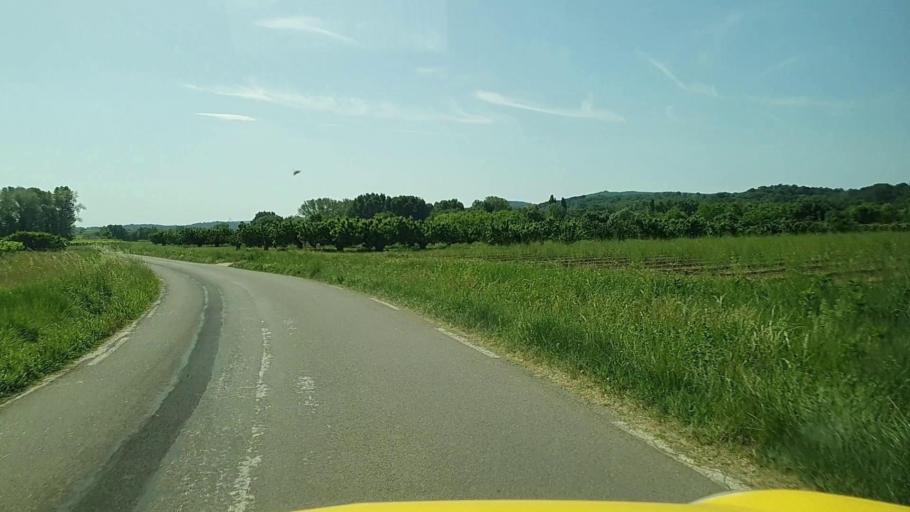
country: FR
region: Languedoc-Roussillon
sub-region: Departement du Gard
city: Sabran
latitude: 44.1070
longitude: 4.5363
